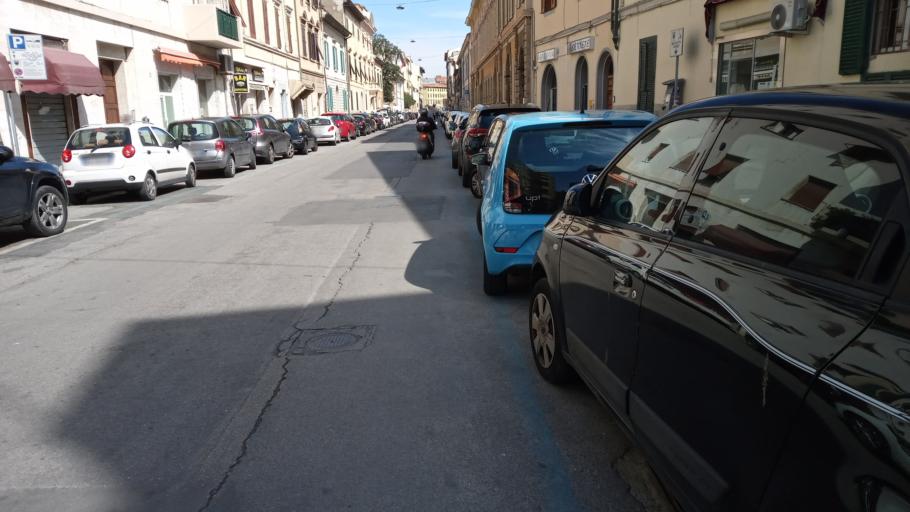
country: IT
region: Tuscany
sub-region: Provincia di Livorno
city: Livorno
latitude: 43.5408
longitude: 10.3129
